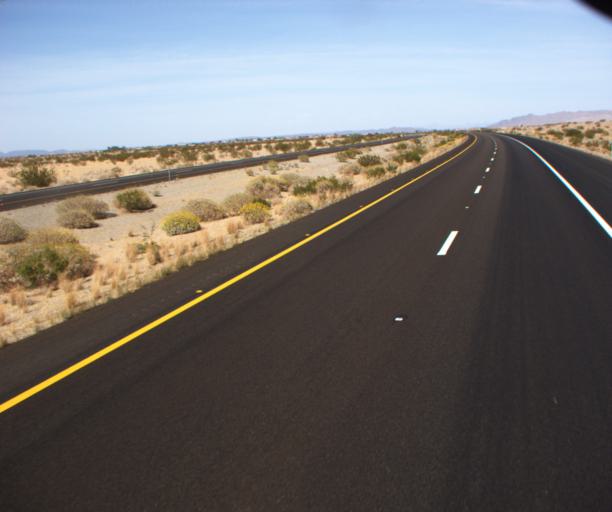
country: US
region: Arizona
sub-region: Yuma County
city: Fortuna Foothills
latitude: 32.6097
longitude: -114.5267
